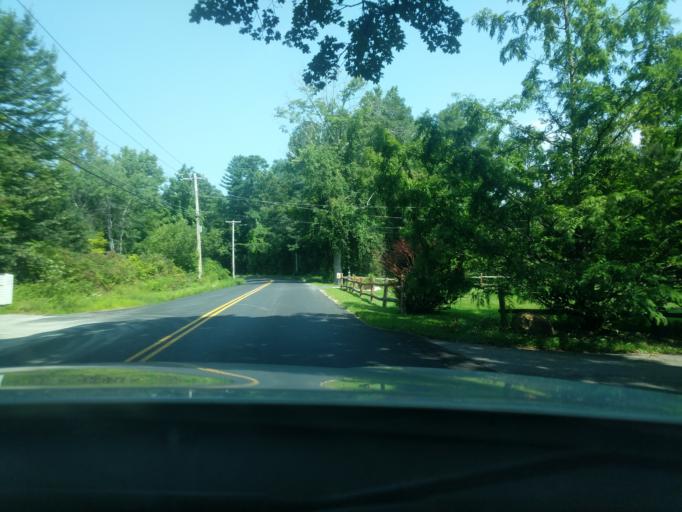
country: US
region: Massachusetts
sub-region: Berkshire County
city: Great Barrington
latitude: 42.2069
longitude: -73.3602
